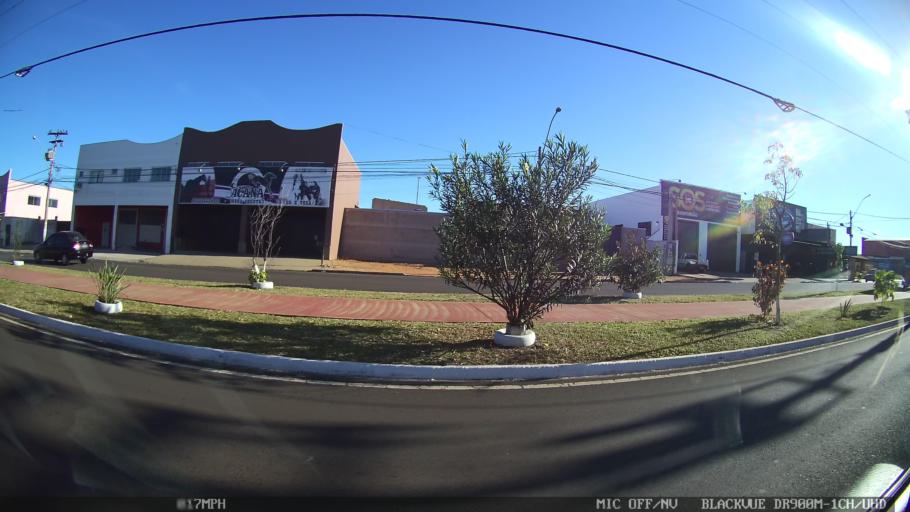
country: BR
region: Sao Paulo
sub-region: Franca
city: Franca
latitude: -20.5726
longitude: -47.3705
